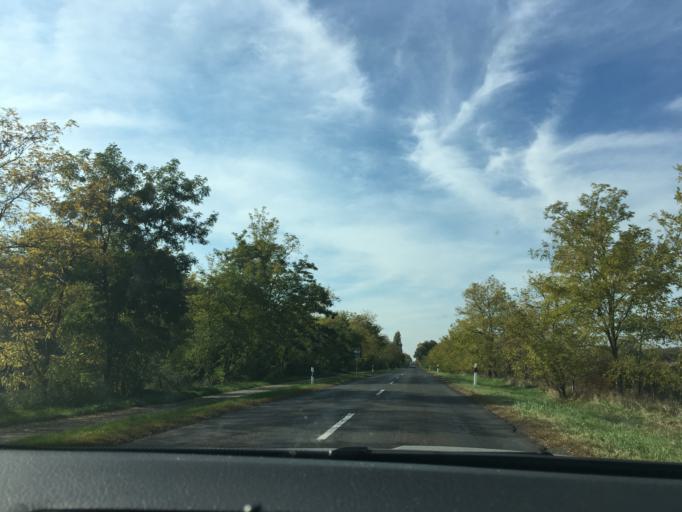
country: HU
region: Hajdu-Bihar
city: Vamospercs
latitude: 47.5257
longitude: 21.9412
